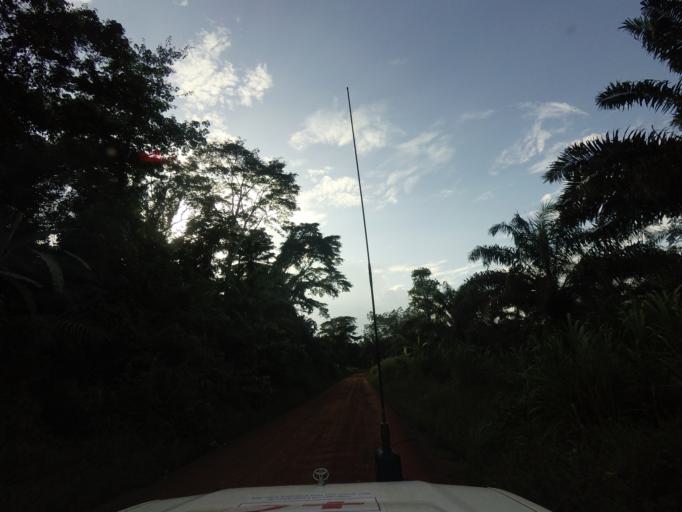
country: GN
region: Nzerekore
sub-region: Nzerekore Prefecture
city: Nzerekore
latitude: 7.6855
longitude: -8.8144
